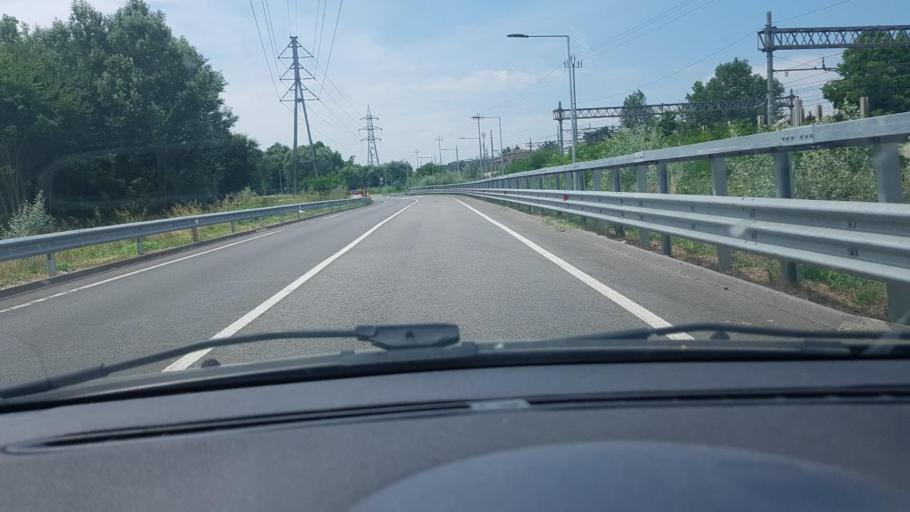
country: IT
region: Veneto
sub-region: Provincia di Padova
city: Cadoneghe
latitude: 45.4225
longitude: 11.9148
